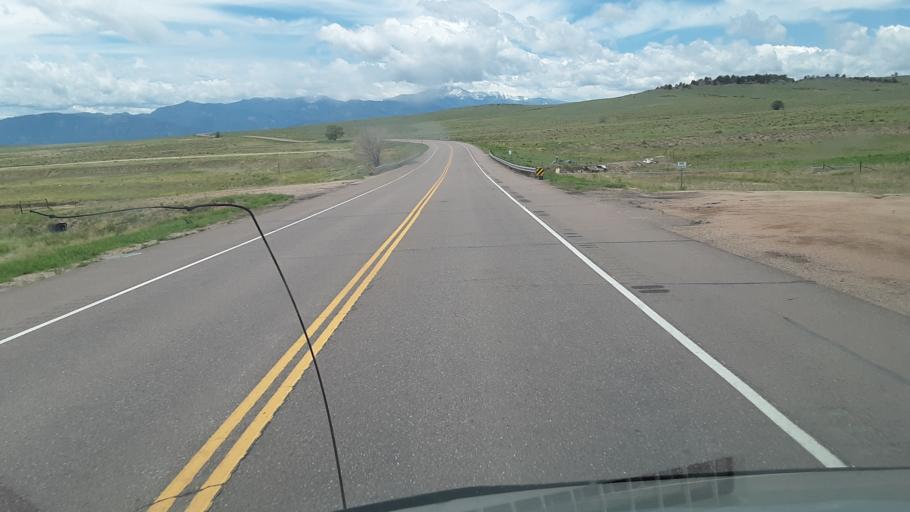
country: US
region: Colorado
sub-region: El Paso County
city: Cimarron Hills
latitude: 38.8390
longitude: -104.6261
